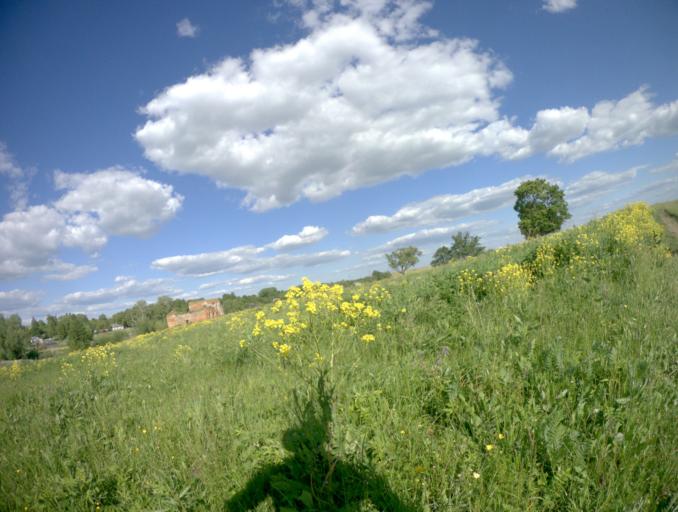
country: RU
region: Vladimir
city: Vladimir
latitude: 56.2971
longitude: 40.2958
